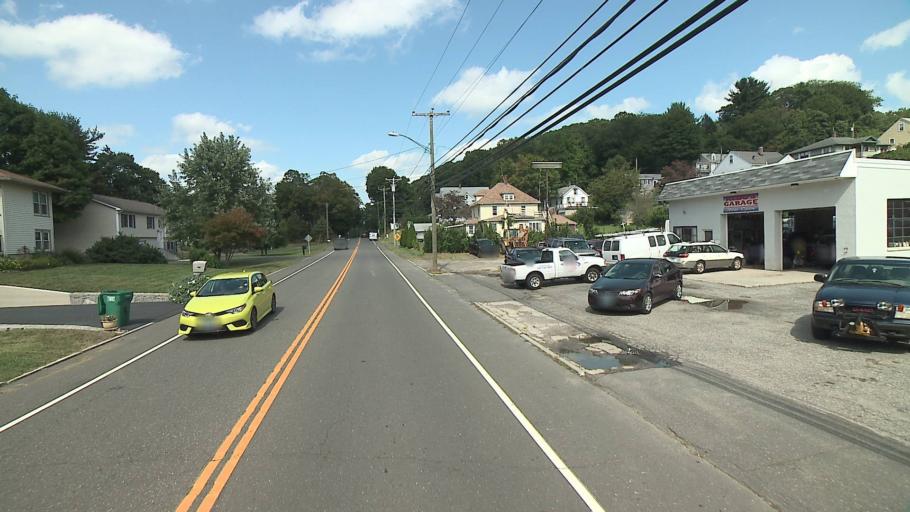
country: US
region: Connecticut
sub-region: New Haven County
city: Seymour
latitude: 41.3809
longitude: -73.0759
